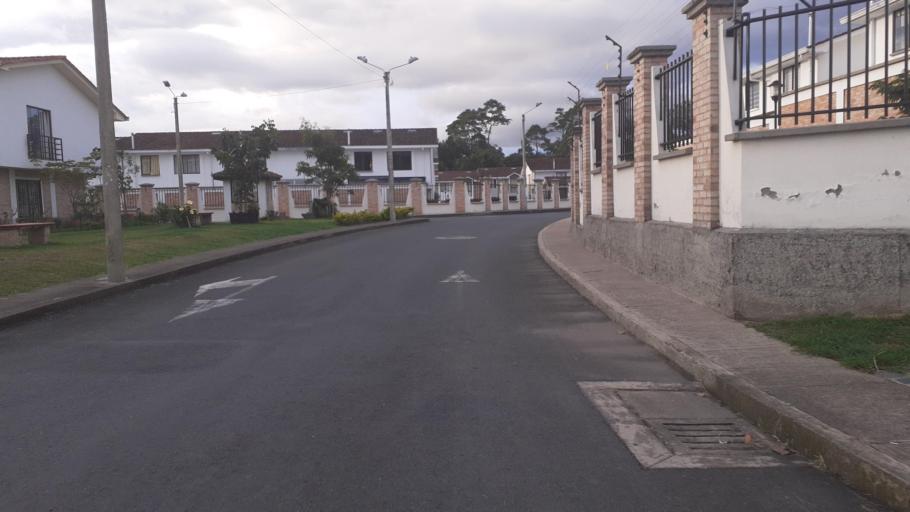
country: CO
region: Cauca
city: Popayan
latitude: 2.4625
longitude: -76.5854
